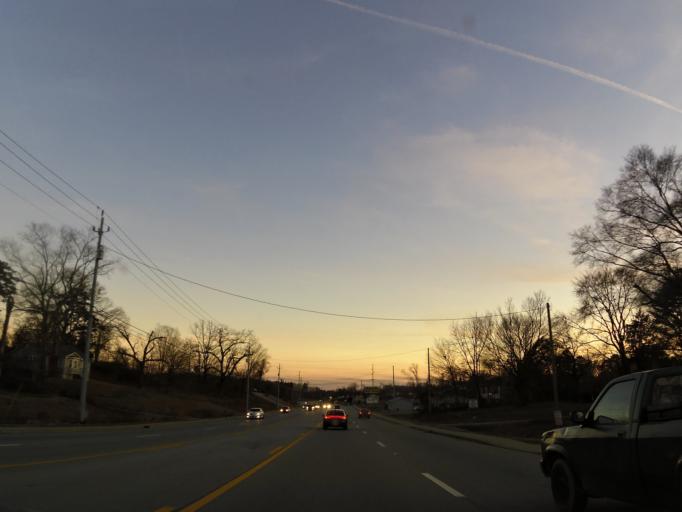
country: US
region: Tennessee
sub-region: Bradley County
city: South Cleveland
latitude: 35.1247
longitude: -84.8647
